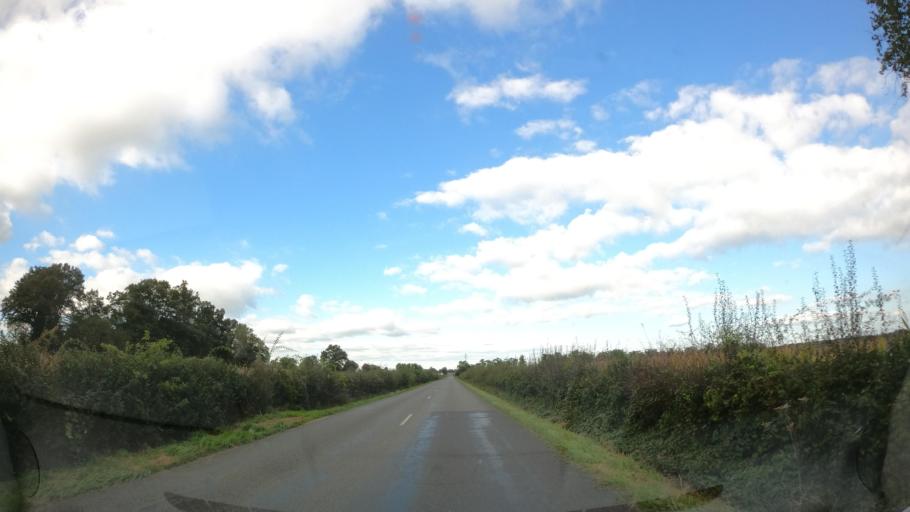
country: FR
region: Auvergne
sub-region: Departement de l'Allier
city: Dompierre-sur-Besbre
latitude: 46.4890
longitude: 3.6570
